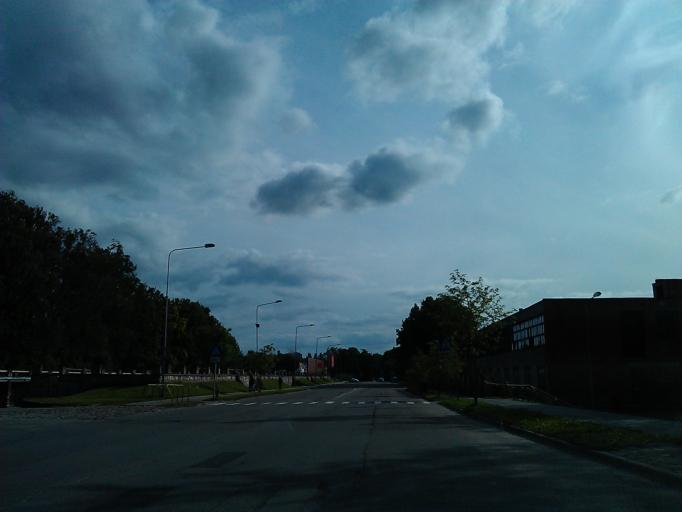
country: LV
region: Cesu Rajons
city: Cesis
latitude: 57.3121
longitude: 25.2797
